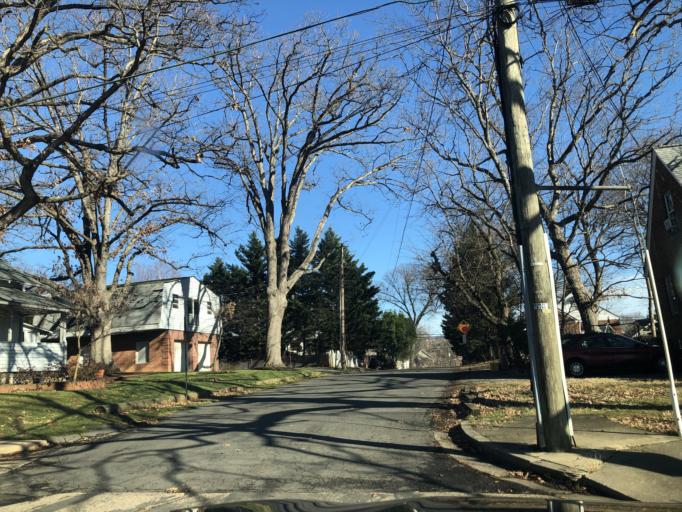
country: US
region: Virginia
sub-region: Arlington County
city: Arlington
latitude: 38.8872
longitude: -77.1152
